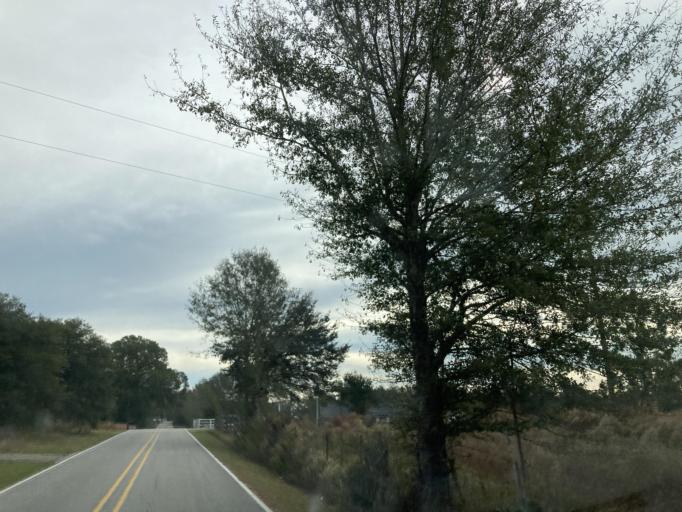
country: US
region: Mississippi
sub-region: Lamar County
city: Purvis
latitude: 31.1128
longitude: -89.4789
